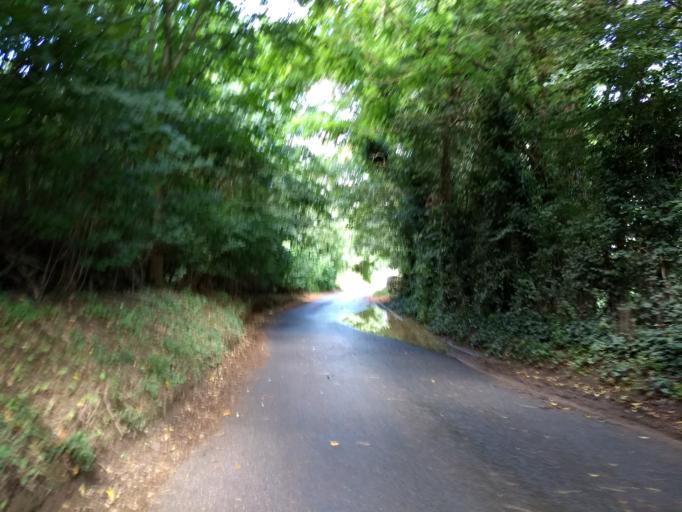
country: GB
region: England
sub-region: Isle of Wight
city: Newport
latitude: 50.6800
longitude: -1.2936
